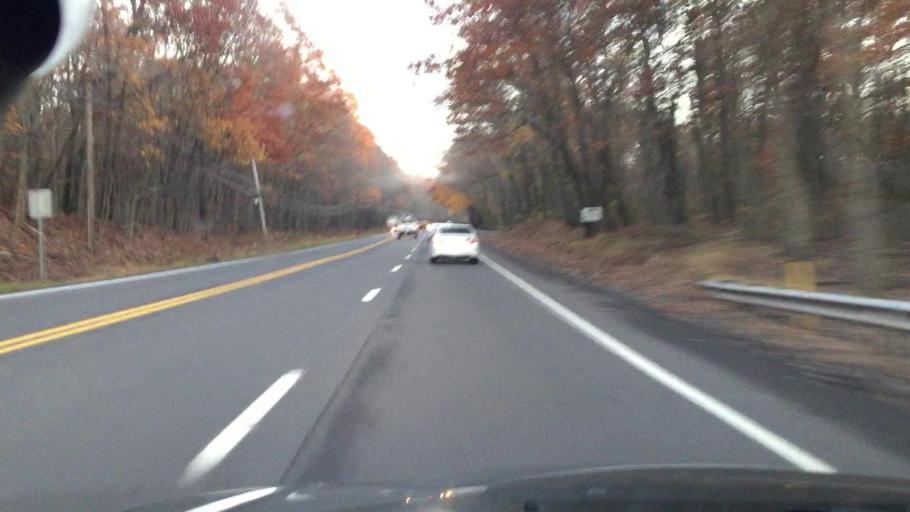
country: US
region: Pennsylvania
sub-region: Luzerne County
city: Freeland
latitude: 41.0647
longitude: -75.9633
